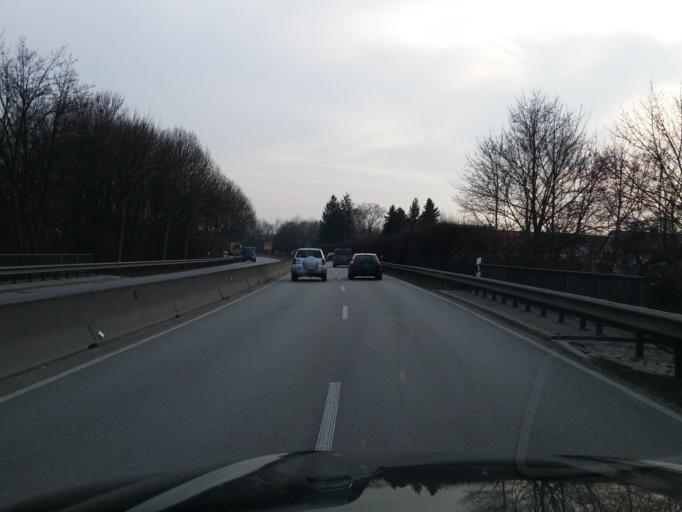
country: DE
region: Bavaria
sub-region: Lower Bavaria
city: Ergolding
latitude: 48.5576
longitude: 12.1632
